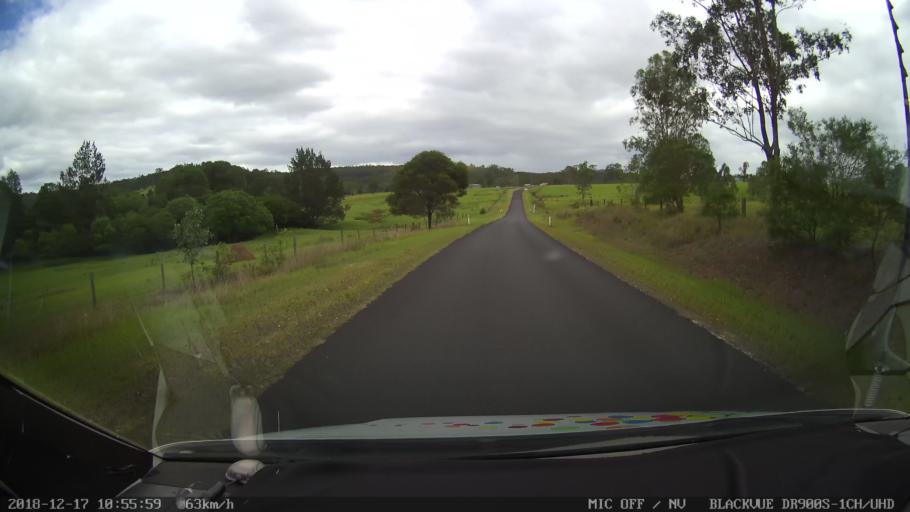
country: AU
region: New South Wales
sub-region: Richmond Valley
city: Casino
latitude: -28.8252
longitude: 152.5843
